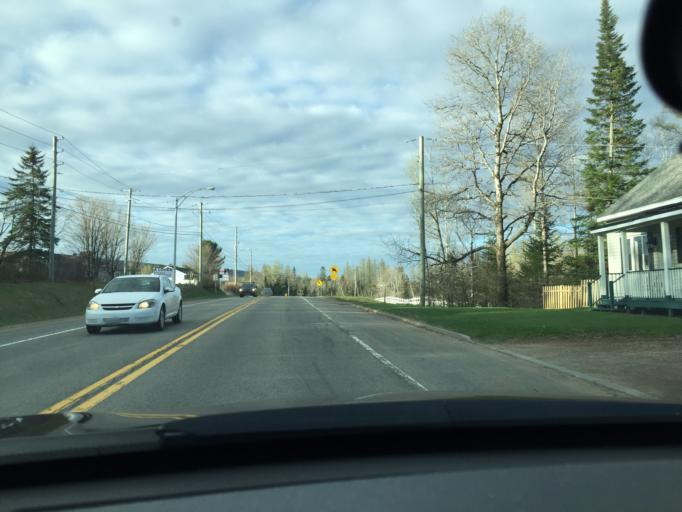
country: CA
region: Quebec
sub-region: Capitale-Nationale
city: Shannon
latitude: 46.8758
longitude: -71.5227
